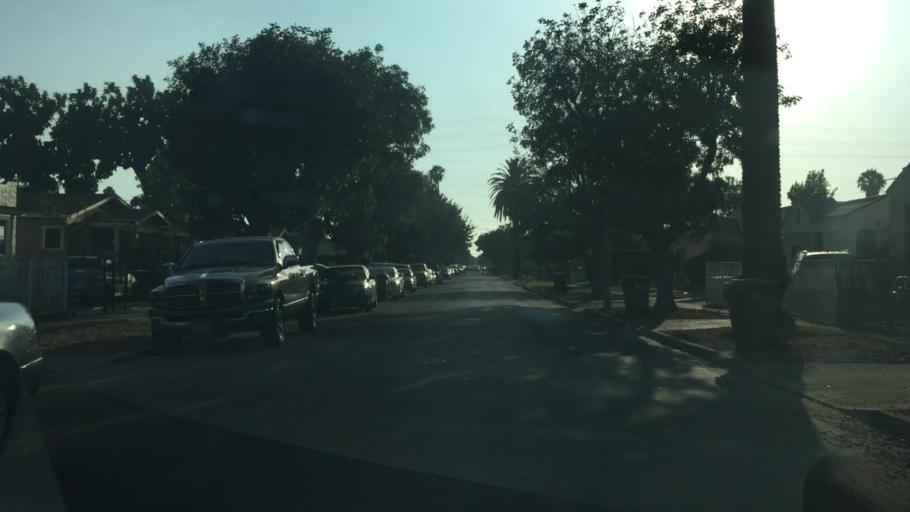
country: US
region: California
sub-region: Los Angeles County
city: Florence-Graham
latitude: 33.9638
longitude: -118.2619
